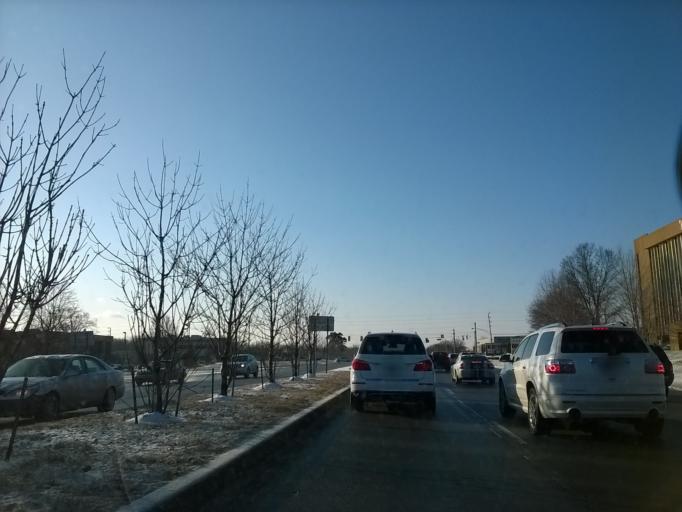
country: US
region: Indiana
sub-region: Marion County
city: Meridian Hills
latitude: 39.9211
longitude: -86.1580
